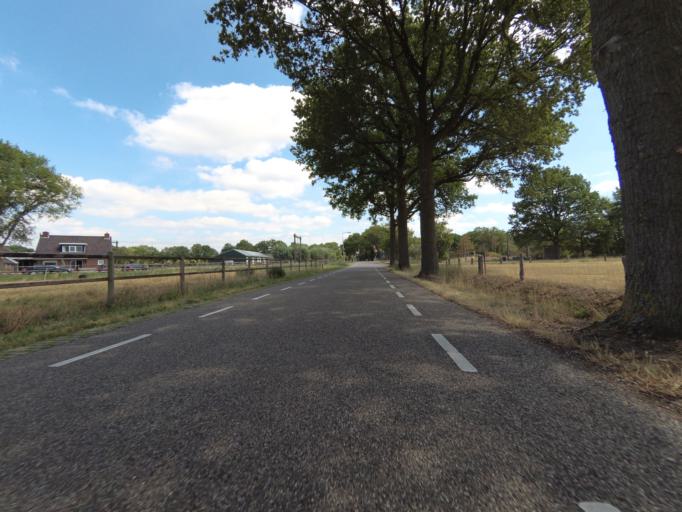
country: NL
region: Overijssel
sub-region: Gemeente Wierden
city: Wierden
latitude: 52.3532
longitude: 6.5692
